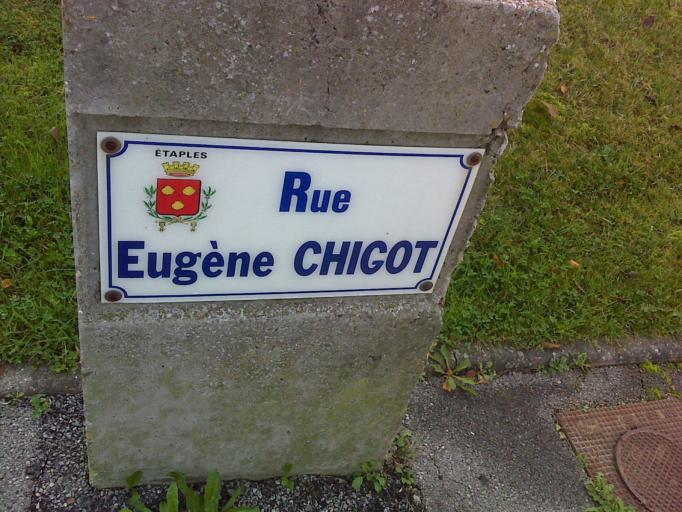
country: FR
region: Nord-Pas-de-Calais
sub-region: Departement du Pas-de-Calais
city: Etaples
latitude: 50.5164
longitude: 1.6532
